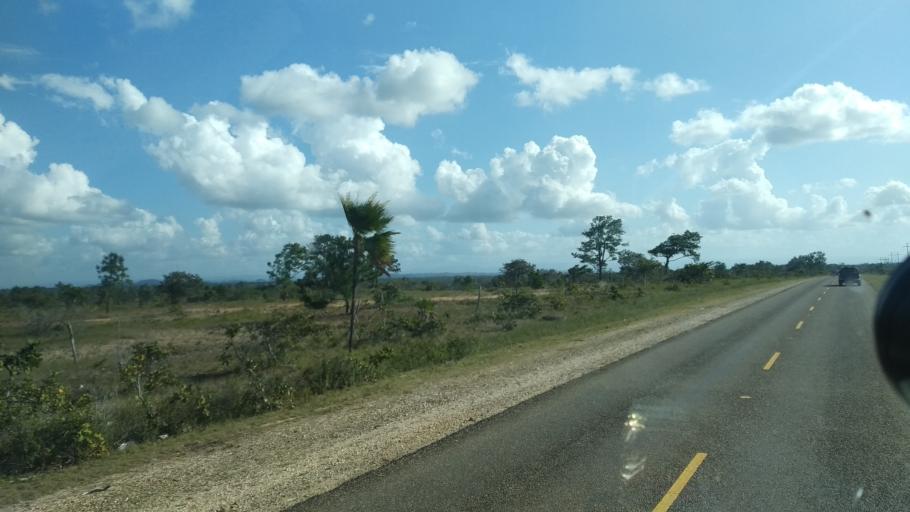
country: BZ
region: Cayo
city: Belmopan
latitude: 17.3890
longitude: -88.5148
